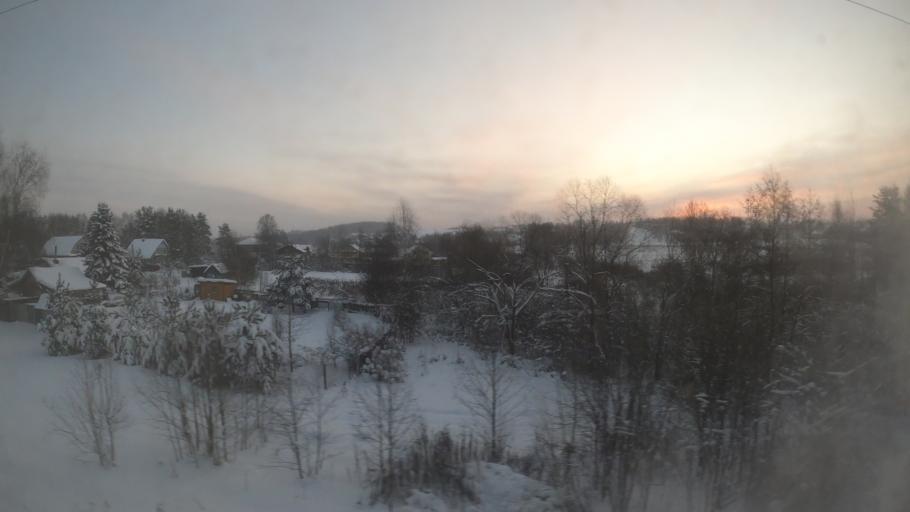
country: RU
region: Moskovskaya
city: Lugovaya
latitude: 56.0715
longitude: 37.4946
